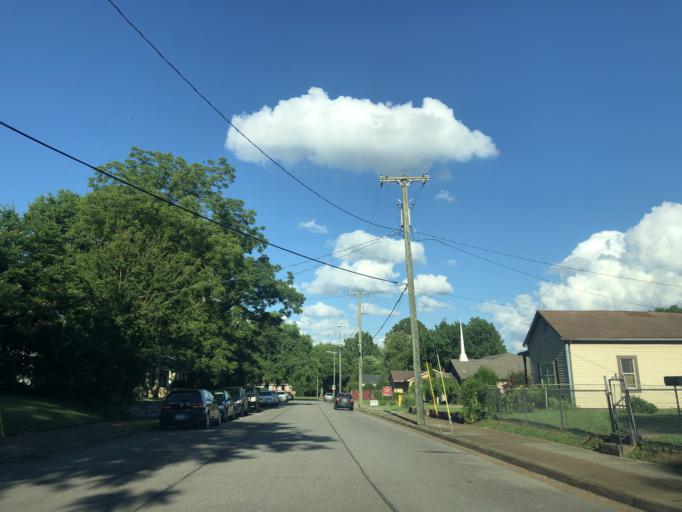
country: US
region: Tennessee
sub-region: Davidson County
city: Nashville
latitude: 36.1836
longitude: -86.7666
